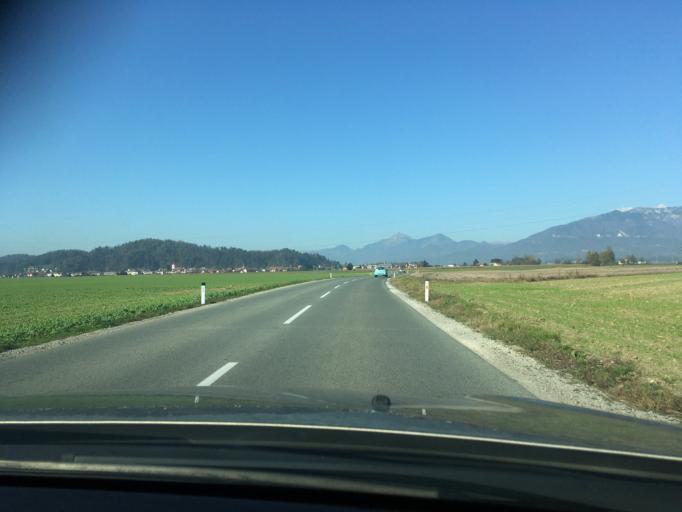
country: SI
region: Domzale
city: Domzale
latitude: 46.1540
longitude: 14.5875
